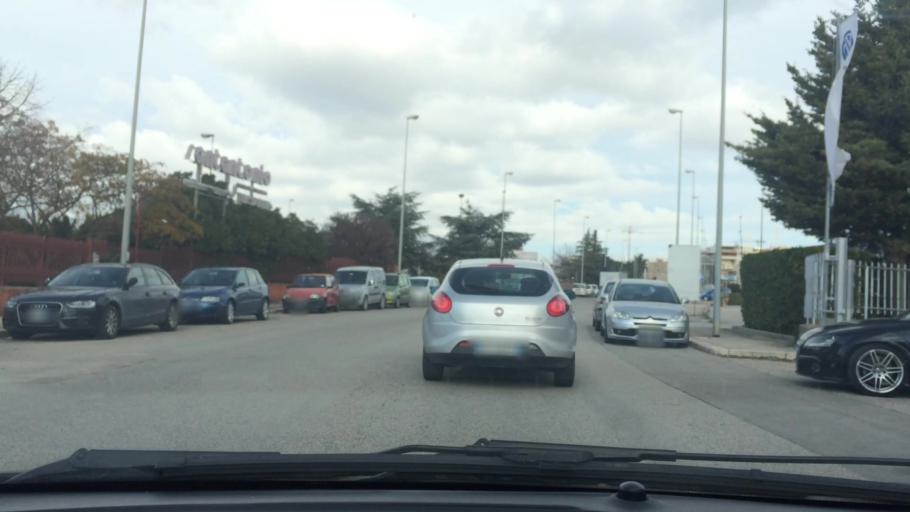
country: IT
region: Basilicate
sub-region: Provincia di Matera
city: Matera
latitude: 40.6715
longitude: 16.5733
